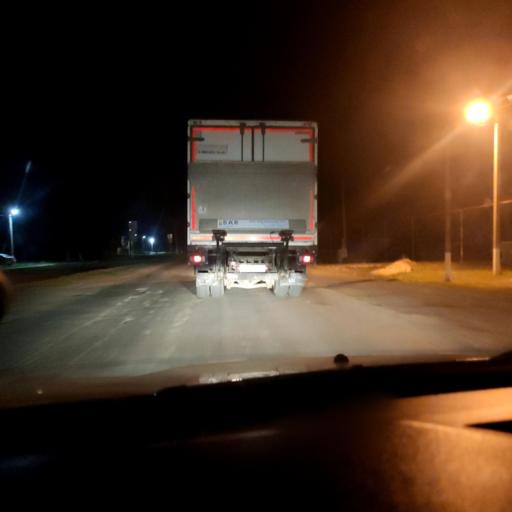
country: RU
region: Samara
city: Spiridonovka
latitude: 53.0899
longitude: 50.6495
